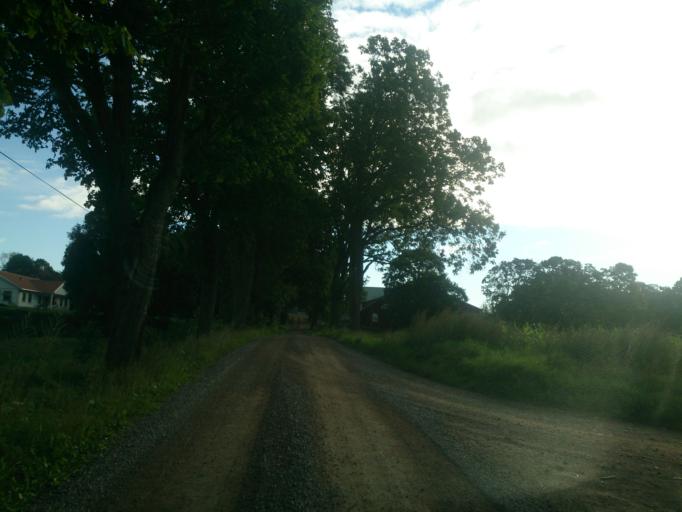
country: SE
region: OEstergoetland
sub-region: Atvidabergs Kommun
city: Atvidaberg
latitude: 58.2685
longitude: 15.9324
